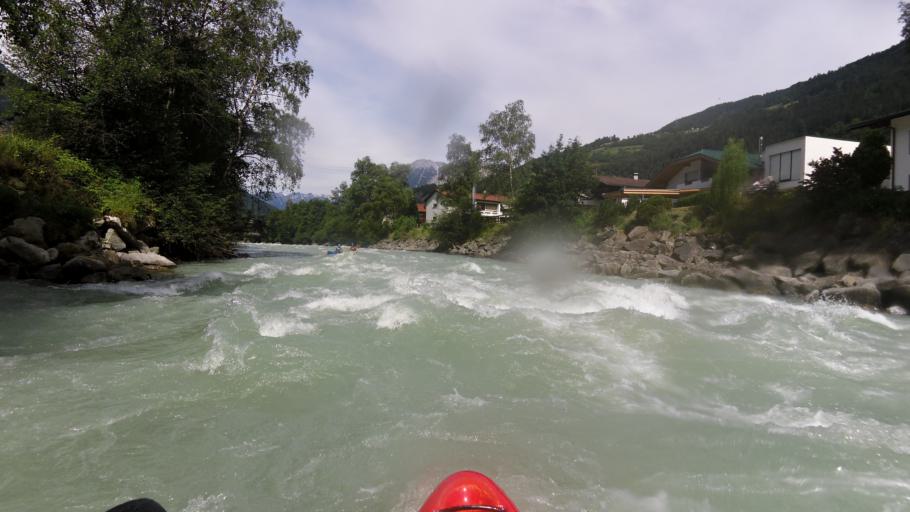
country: AT
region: Tyrol
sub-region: Politischer Bezirk Imst
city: Oetz
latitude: 47.2019
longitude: 10.8957
